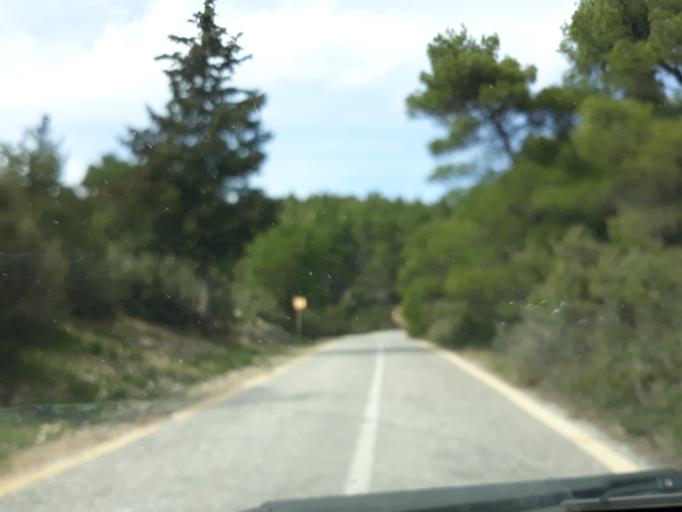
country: GR
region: Attica
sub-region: Nomarchia Anatolikis Attikis
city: Varybobi
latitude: 38.1658
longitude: 23.7921
